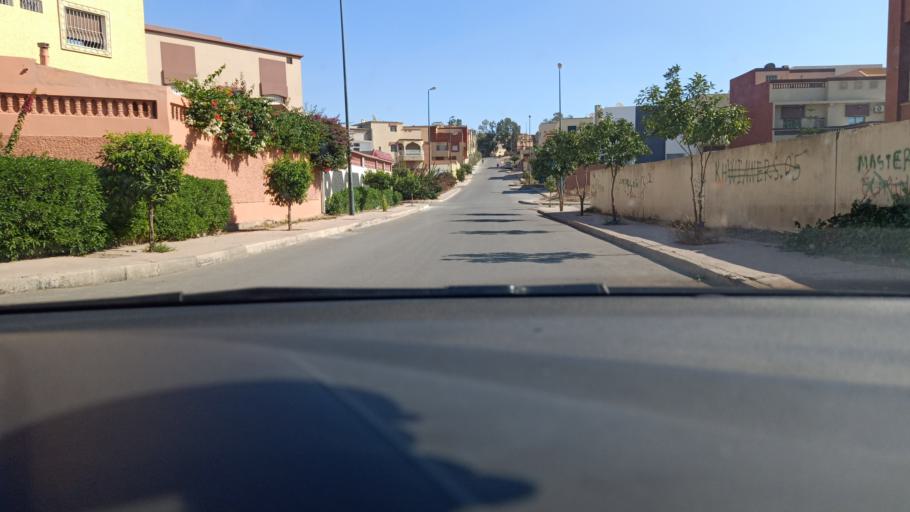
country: MA
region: Doukkala-Abda
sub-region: Safi
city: Youssoufia
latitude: 32.2423
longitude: -8.5325
